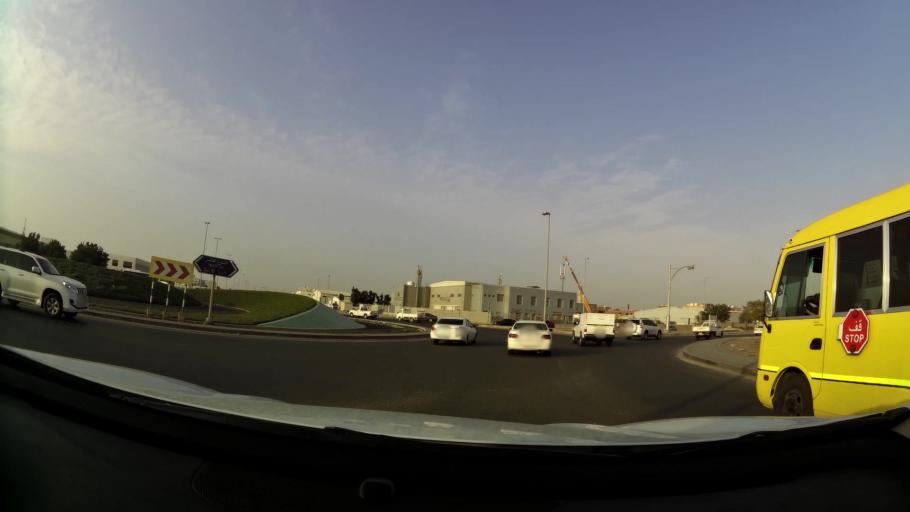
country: AE
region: Abu Dhabi
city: Abu Dhabi
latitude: 24.3680
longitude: 54.5015
